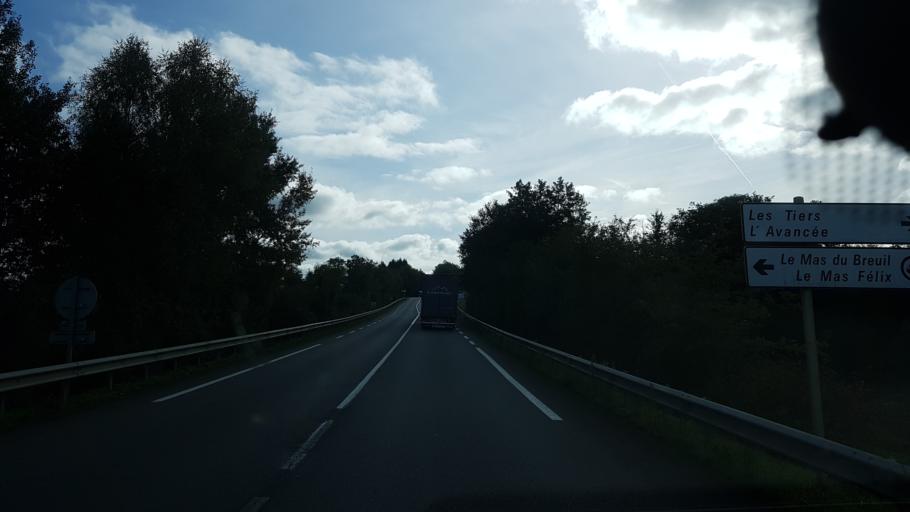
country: FR
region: Poitou-Charentes
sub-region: Departement de la Charente
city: Confolens
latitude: 46.0360
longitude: 0.6588
